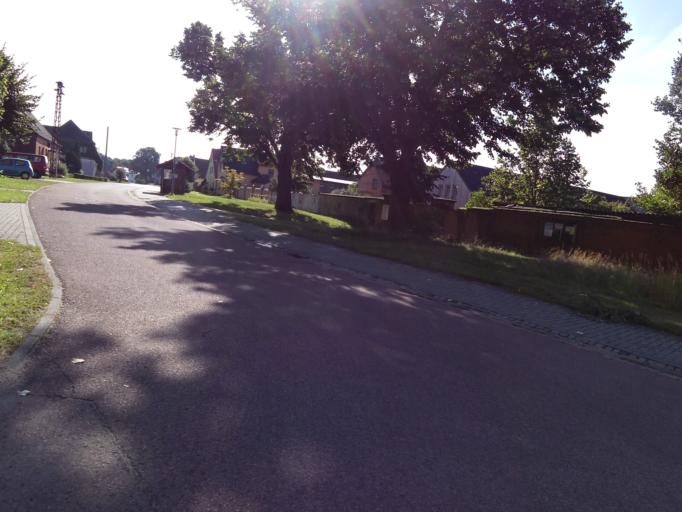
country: DE
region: Saxony-Anhalt
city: Coswig
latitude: 51.8816
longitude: 12.5070
